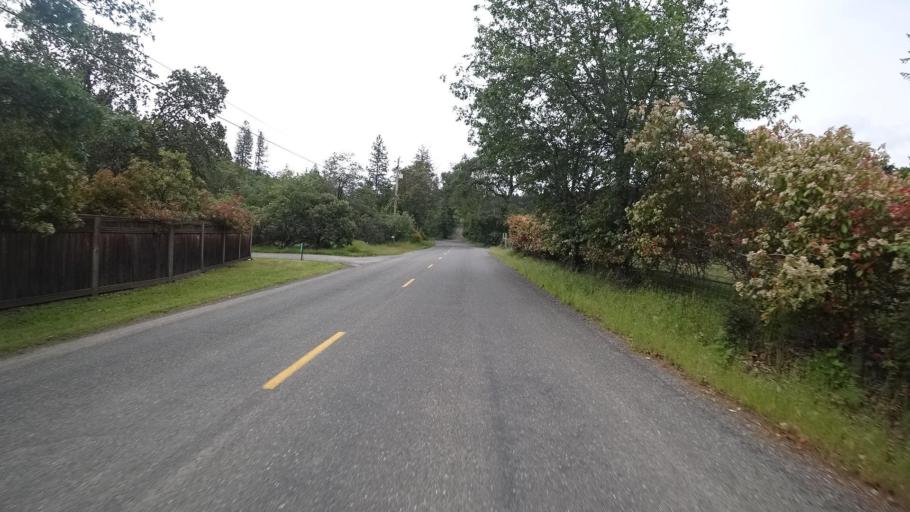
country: US
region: California
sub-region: Humboldt County
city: Willow Creek
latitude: 40.9602
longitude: -123.6303
